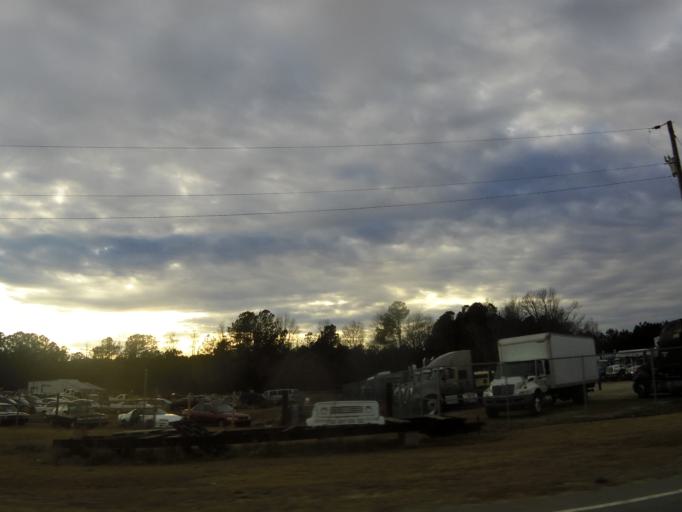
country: US
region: North Carolina
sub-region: Nash County
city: Sharpsburg
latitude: 35.9011
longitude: -77.8264
